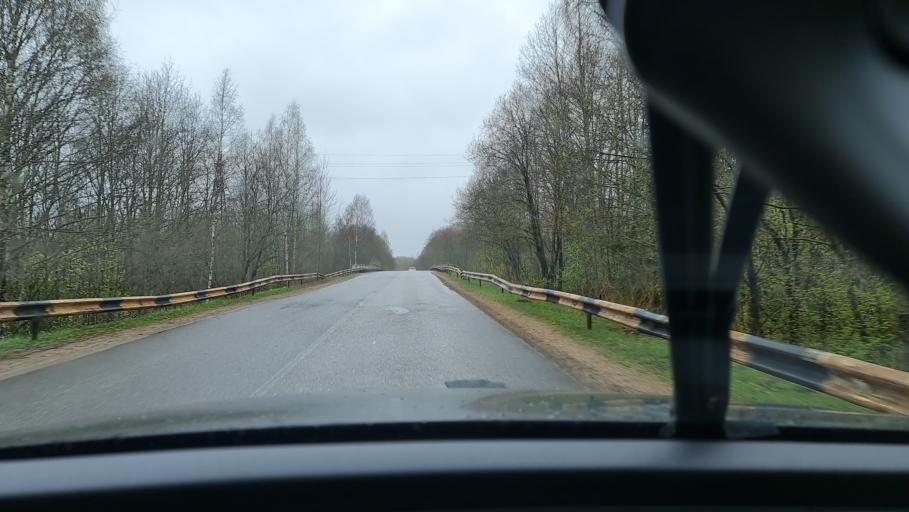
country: RU
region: Novgorod
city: Kresttsy
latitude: 57.9703
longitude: 32.7194
